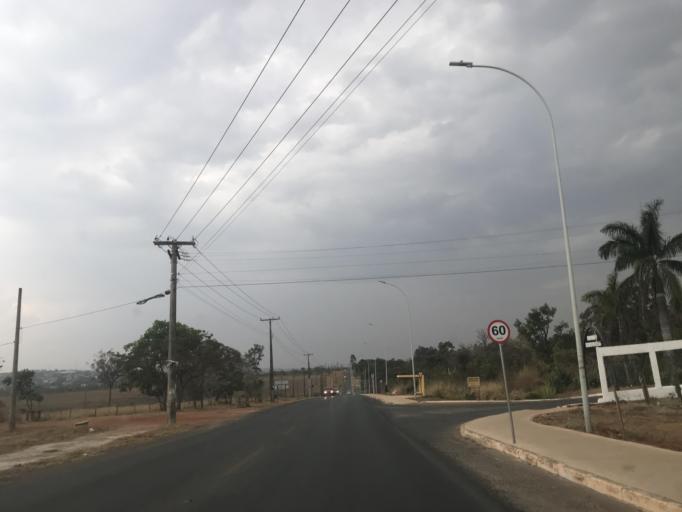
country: BR
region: Federal District
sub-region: Brasilia
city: Brasilia
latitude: -15.6627
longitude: -47.8308
